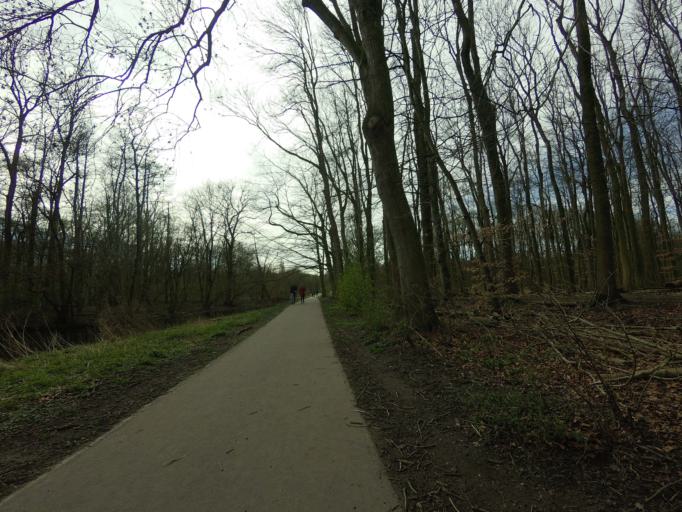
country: NL
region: North Holland
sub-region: Gemeente Amstelveen
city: Amstelveen
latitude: 52.3013
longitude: 4.8223
